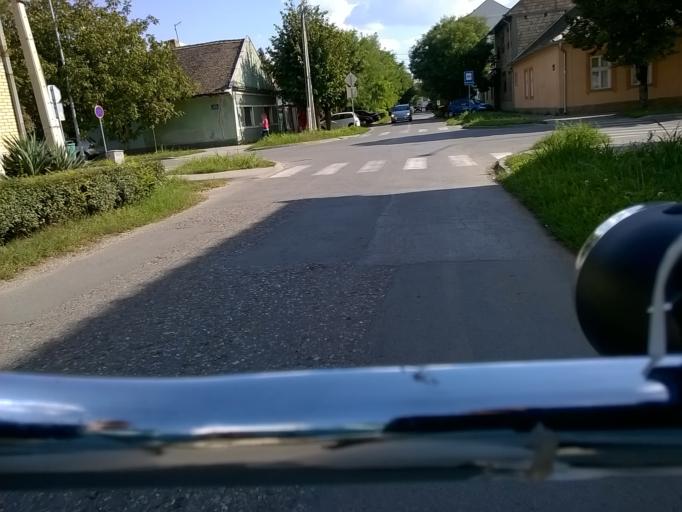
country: RS
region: Autonomna Pokrajina Vojvodina
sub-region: Juznobanatski Okrug
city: Pancevo
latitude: 44.8765
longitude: 20.6447
